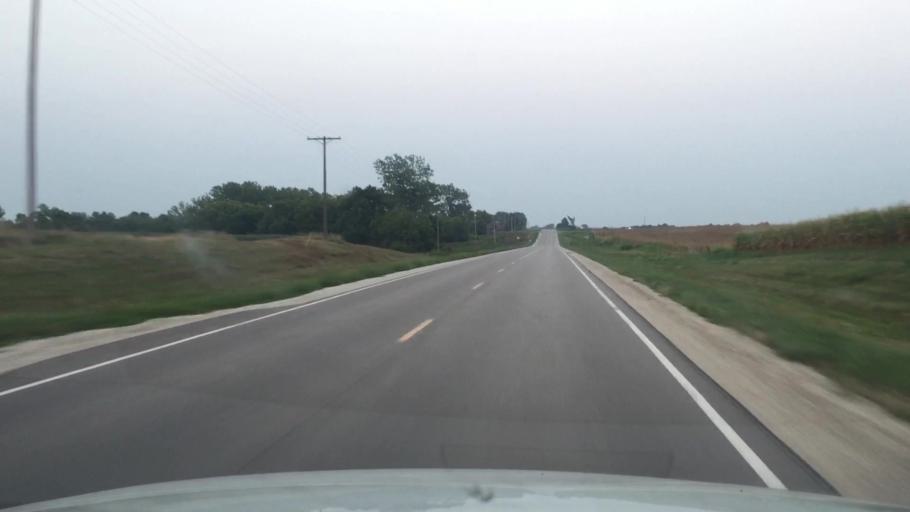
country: US
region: Iowa
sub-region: Warren County
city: Indianola
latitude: 41.1826
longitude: -93.4866
